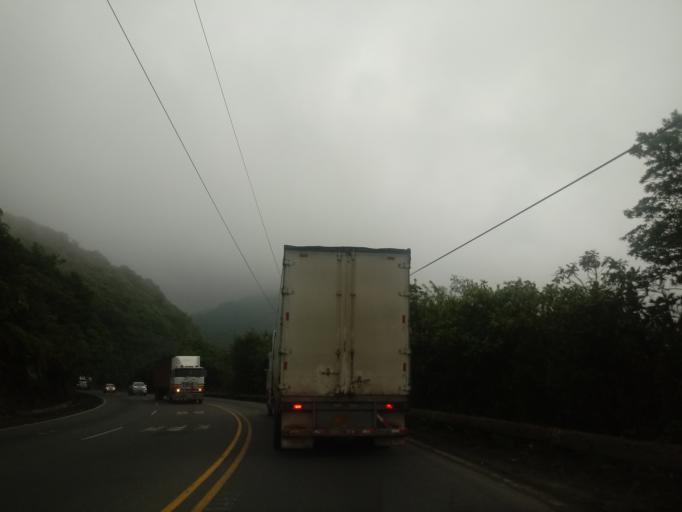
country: CR
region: Heredia
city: Angeles
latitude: 10.0538
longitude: -84.0036
